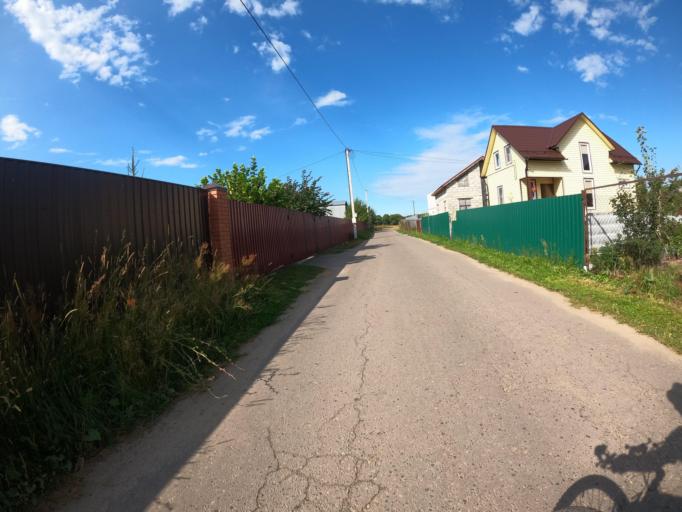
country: RU
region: Moskovskaya
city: Konobeyevo
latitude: 55.3938
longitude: 38.7095
